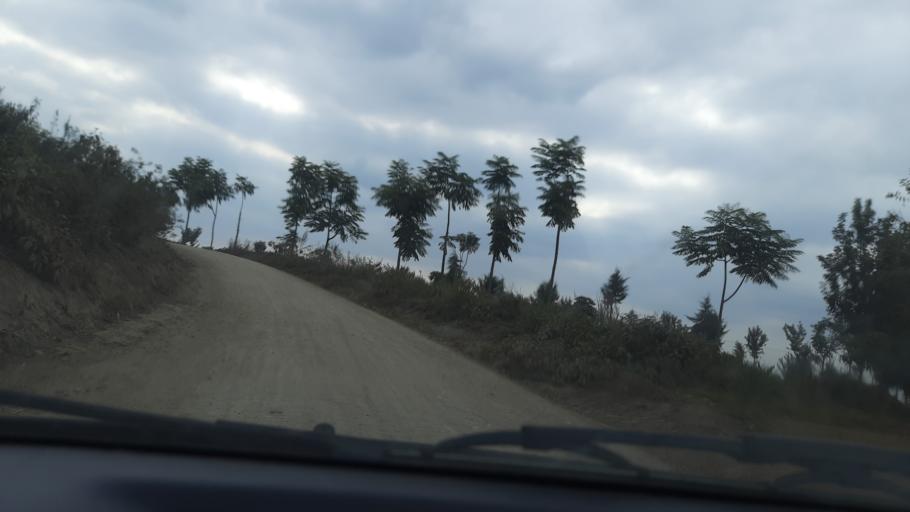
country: TZ
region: Kilimanjaro
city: Moshi
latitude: -2.8716
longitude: 37.3453
